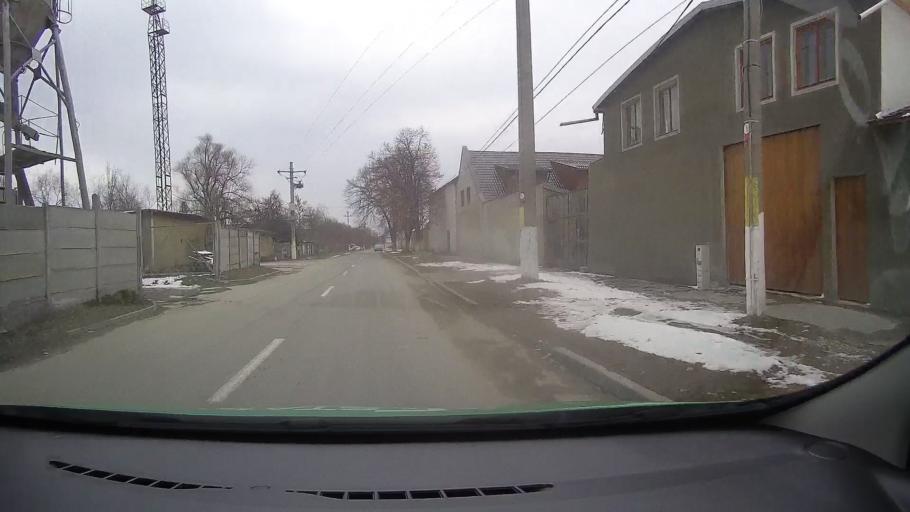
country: RO
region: Brasov
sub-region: Comuna Cristian
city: Cristian
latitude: 45.6216
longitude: 25.4778
